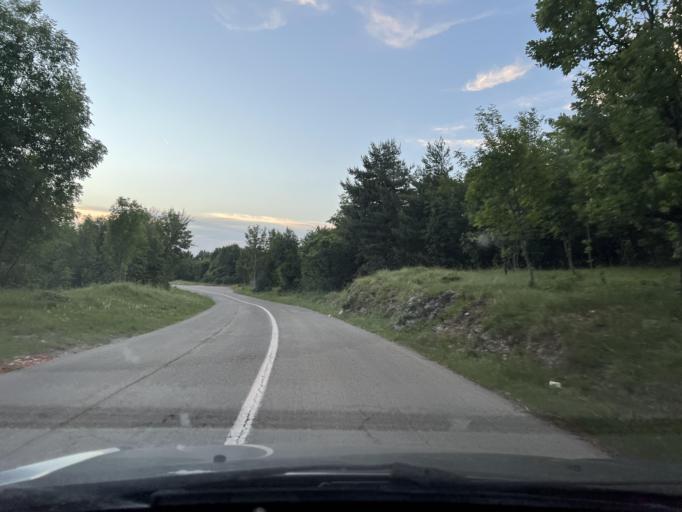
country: HR
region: Primorsko-Goranska
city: Klana
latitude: 45.4725
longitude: 14.2941
